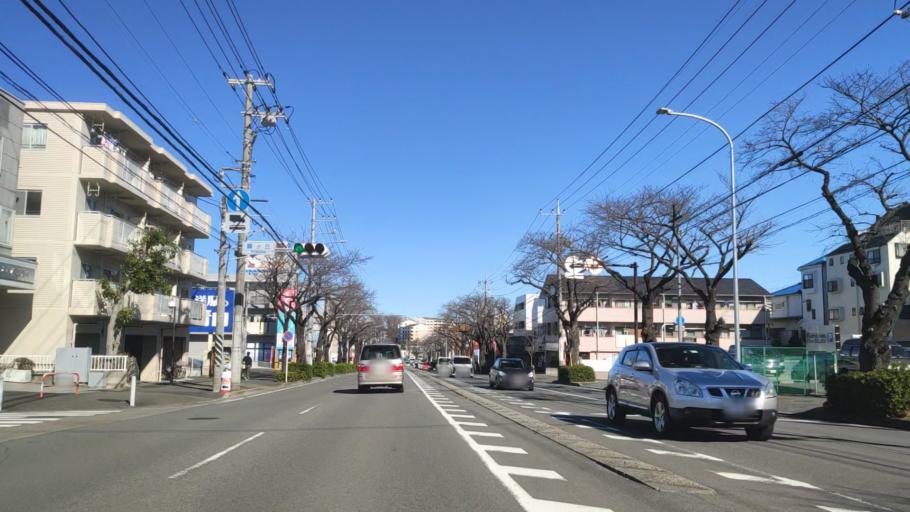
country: JP
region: Tokyo
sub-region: Machida-shi
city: Machida
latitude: 35.5188
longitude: 139.5045
